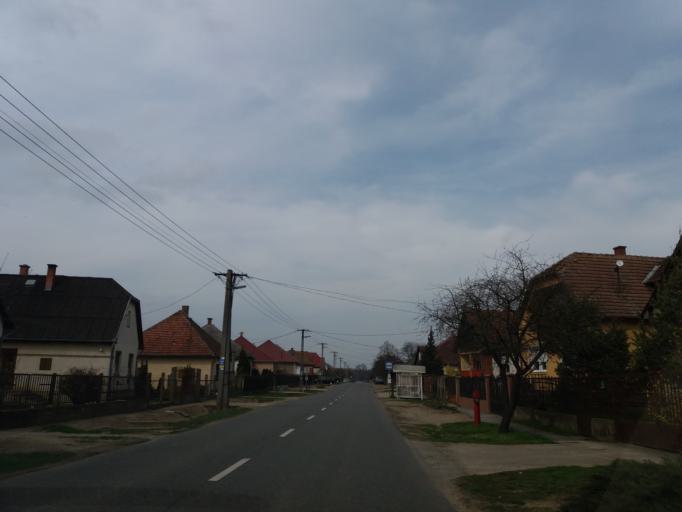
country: HU
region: Szabolcs-Szatmar-Bereg
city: Anarcs
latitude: 48.1801
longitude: 22.1008
